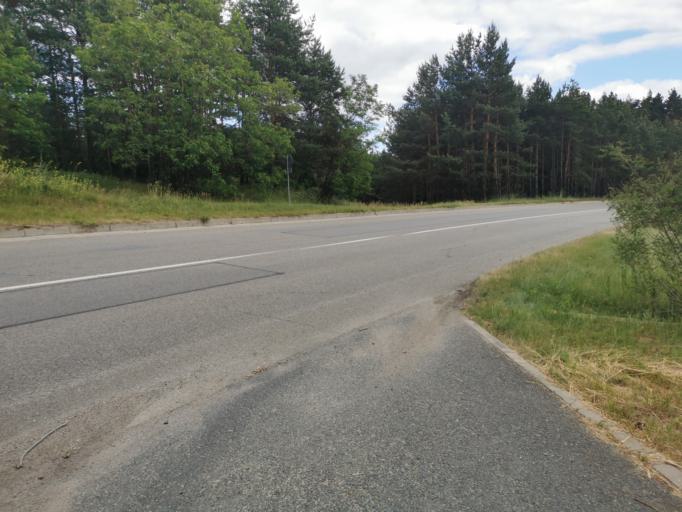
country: CZ
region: South Moravian
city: Bzenec
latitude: 48.9410
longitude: 17.2945
